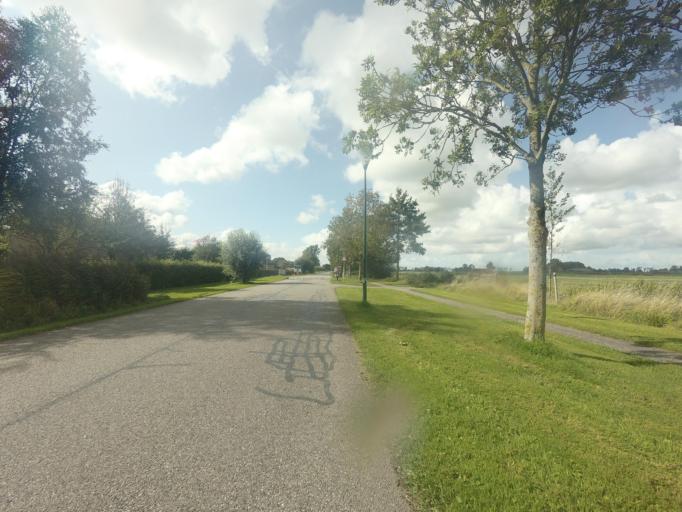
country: NL
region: Friesland
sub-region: Sudwest Fryslan
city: Bolsward
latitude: 53.0523
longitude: 5.5716
